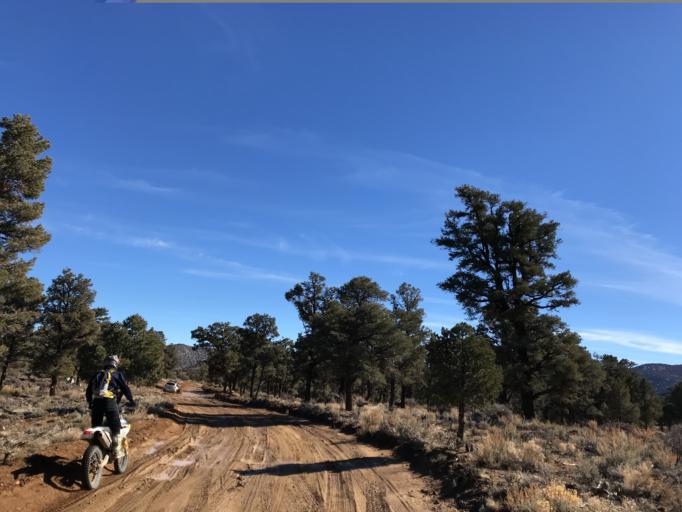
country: US
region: California
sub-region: San Bernardino County
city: Big Bear City
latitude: 34.2656
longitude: -116.7590
